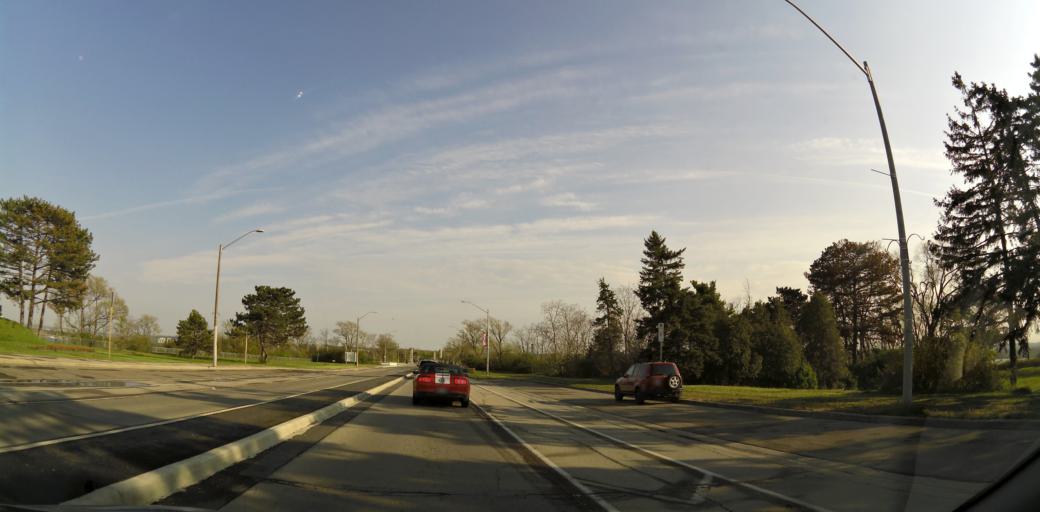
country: CA
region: Ontario
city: Hamilton
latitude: 43.2840
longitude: -79.8923
